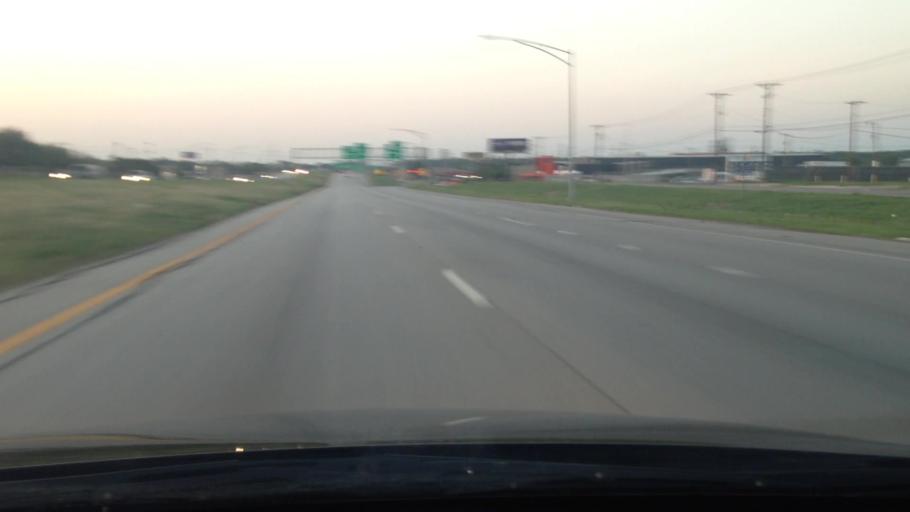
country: US
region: Texas
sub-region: Tarrant County
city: Forest Hill
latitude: 32.7248
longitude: -97.2251
